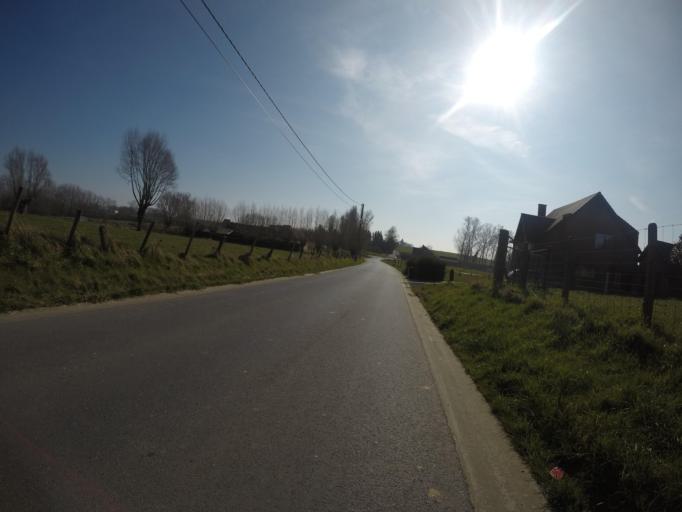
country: BE
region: Flanders
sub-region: Provincie Oost-Vlaanderen
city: Sint-Maria-Lierde
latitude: 50.7906
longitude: 3.8502
